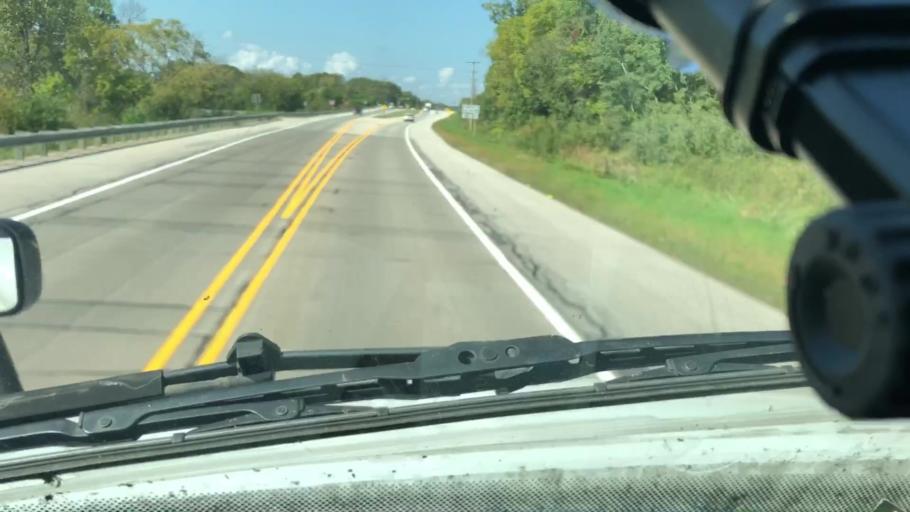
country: US
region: Minnesota
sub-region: Winona County
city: Winona
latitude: 44.0718
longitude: -91.6256
